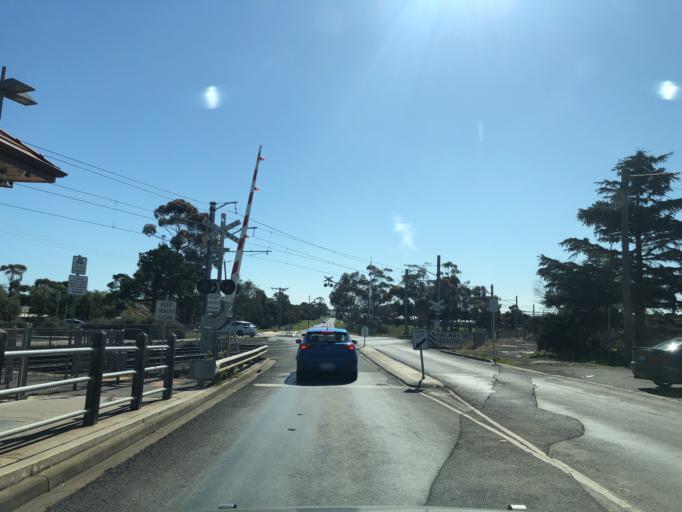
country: AU
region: Victoria
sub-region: Hume
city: Diggers Rest
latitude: -37.6271
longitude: 144.7202
